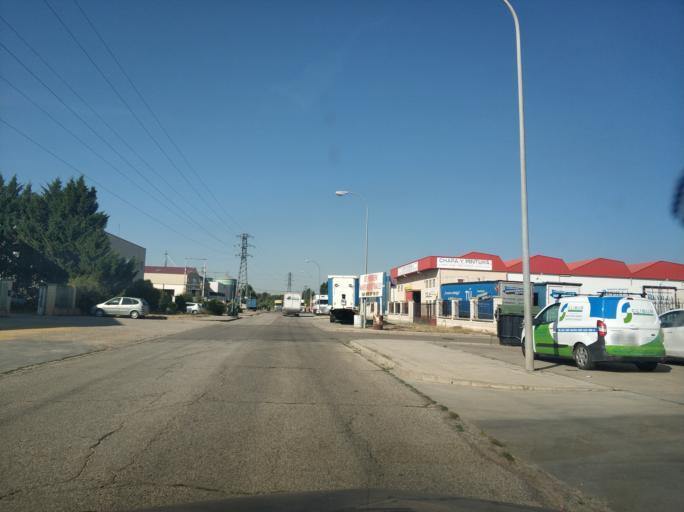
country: ES
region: Castille and Leon
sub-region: Provincia de Burgos
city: Aranda de Duero
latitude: 41.6718
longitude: -3.7081
